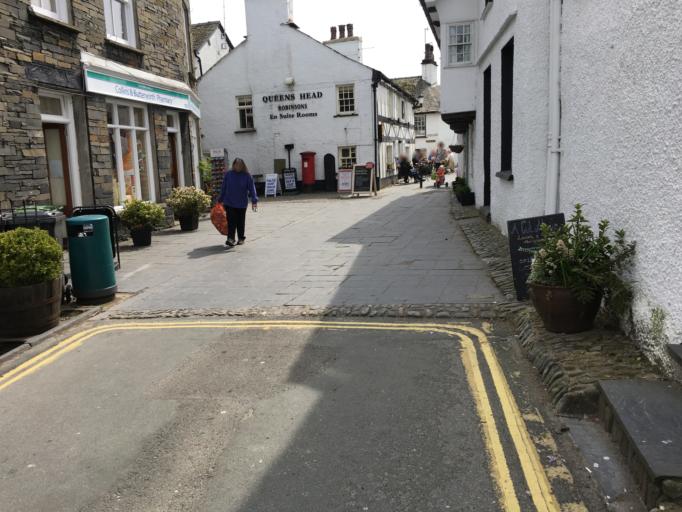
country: GB
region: England
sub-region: Cumbria
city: Ambleside
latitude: 54.3748
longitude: -2.9992
